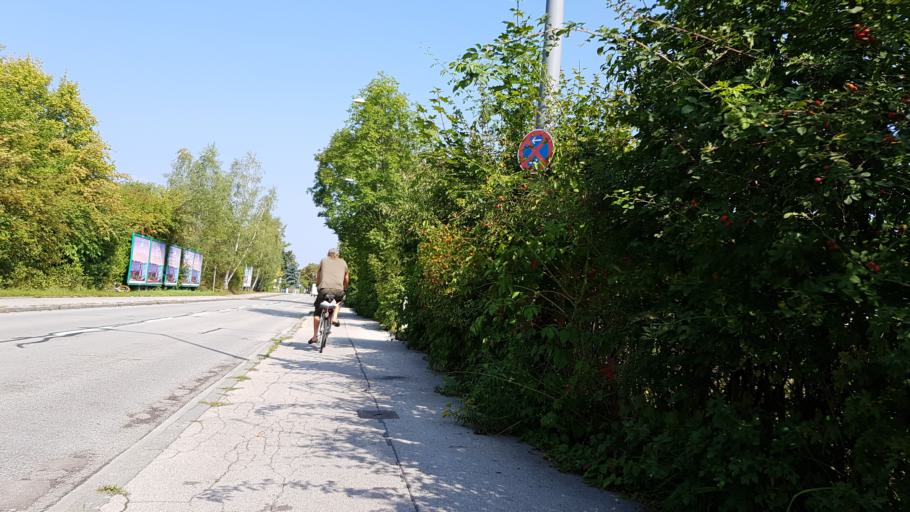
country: DE
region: Bavaria
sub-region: Upper Bavaria
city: Oberschleissheim
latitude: 48.1914
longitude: 11.5342
